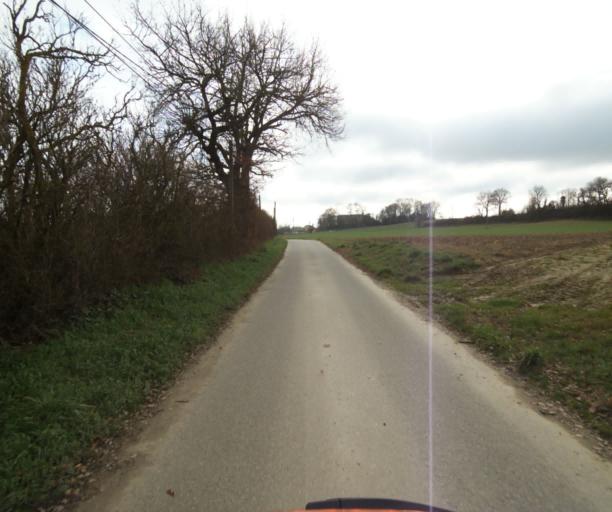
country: FR
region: Languedoc-Roussillon
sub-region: Departement de l'Aude
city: Belpech
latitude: 43.1797
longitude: 1.7340
